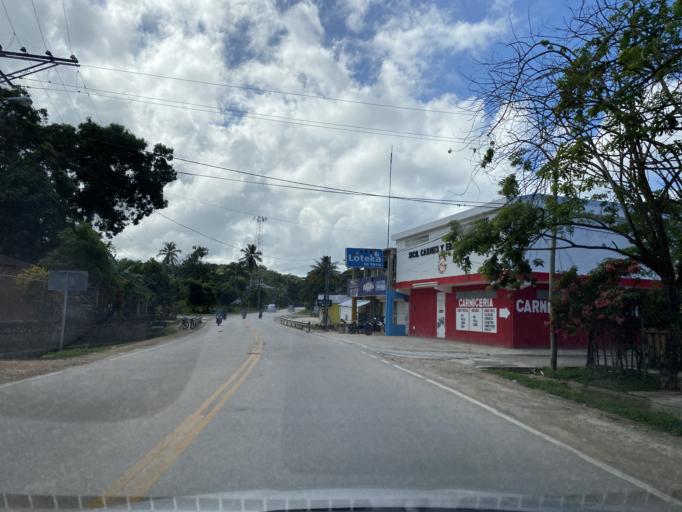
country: DO
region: Samana
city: Las Terrenas
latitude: 19.3070
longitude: -69.5393
